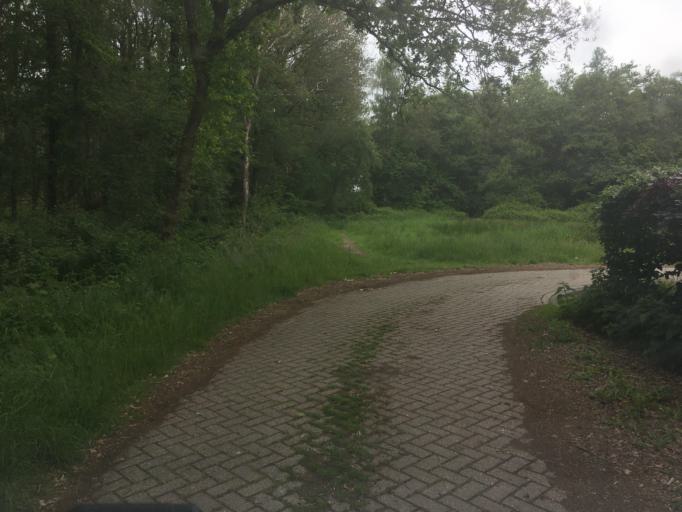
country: NL
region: Friesland
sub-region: Gemeente Heerenveen
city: Nieuwehorne
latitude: 52.9262
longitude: 6.0492
